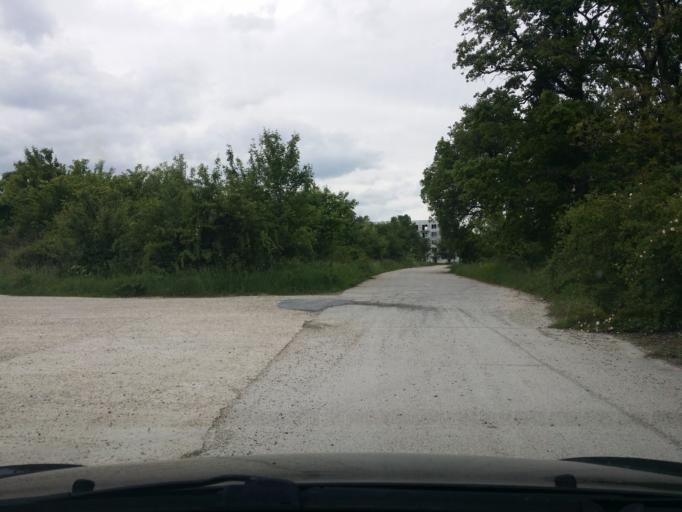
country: HU
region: Veszprem
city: Szentkiralyszabadja
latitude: 47.0793
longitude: 17.9834
